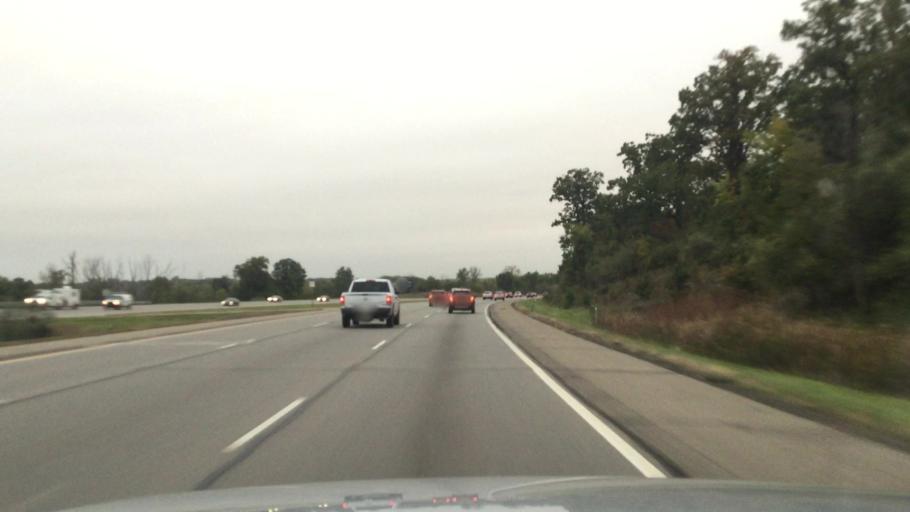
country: US
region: Michigan
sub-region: Oakland County
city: Holly
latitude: 42.8517
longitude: -83.5899
